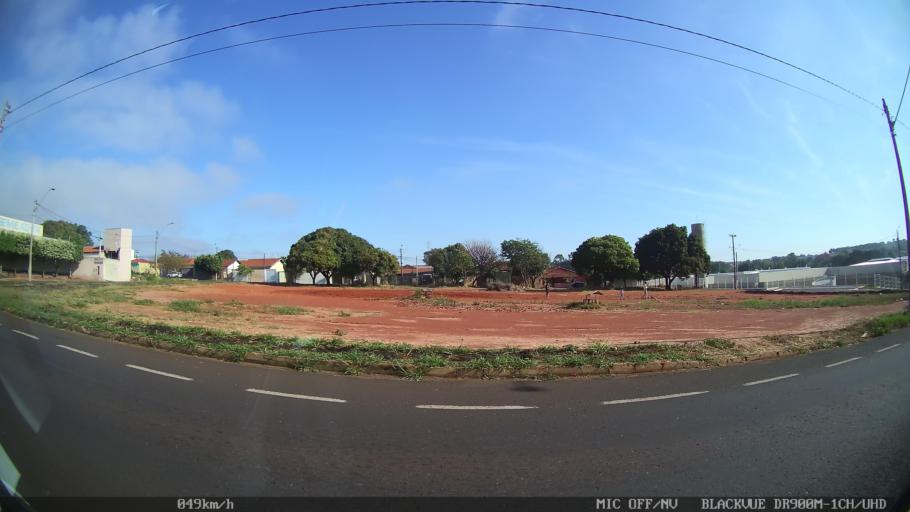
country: BR
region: Sao Paulo
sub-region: Sao Jose Do Rio Preto
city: Sao Jose do Rio Preto
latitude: -20.7908
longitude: -49.4135
